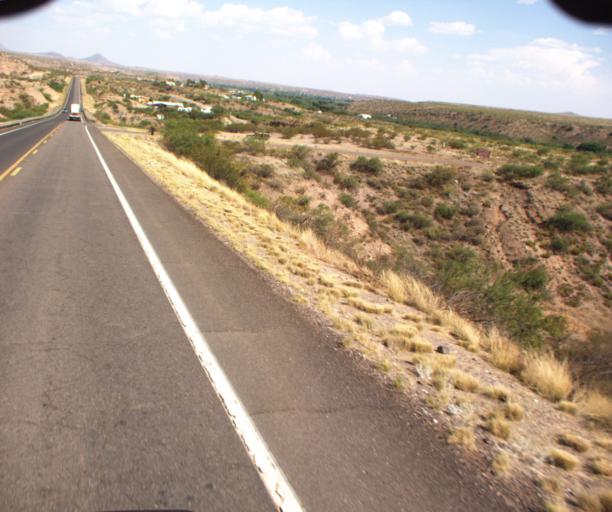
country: US
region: Arizona
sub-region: Greenlee County
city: Clifton
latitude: 32.9428
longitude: -109.2261
